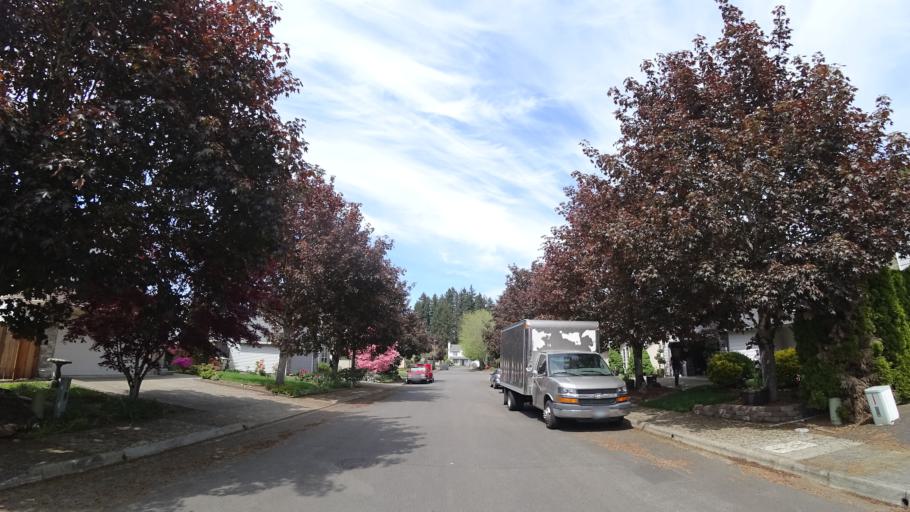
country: US
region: Oregon
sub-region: Washington County
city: Aloha
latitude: 45.4810
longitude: -122.8845
